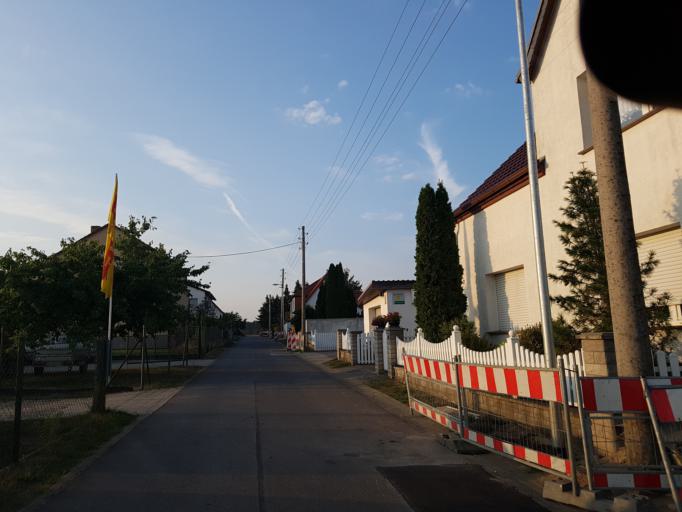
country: DE
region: Brandenburg
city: Plessa
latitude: 51.5332
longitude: 13.6374
